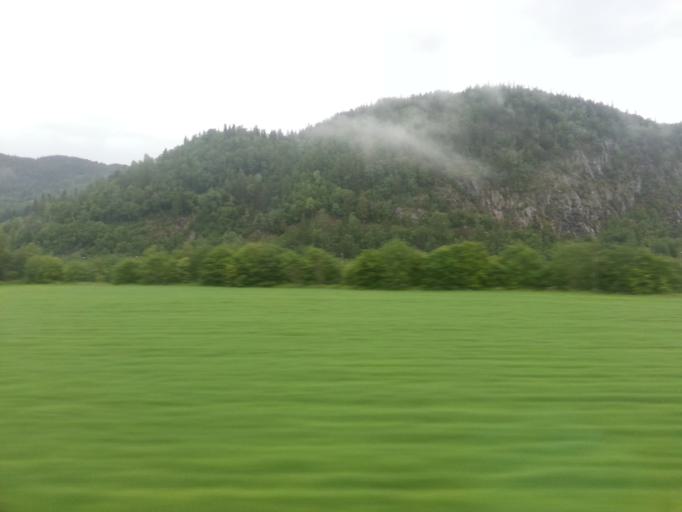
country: NO
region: Sor-Trondelag
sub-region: Midtre Gauldal
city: Storen
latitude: 63.0847
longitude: 10.2461
